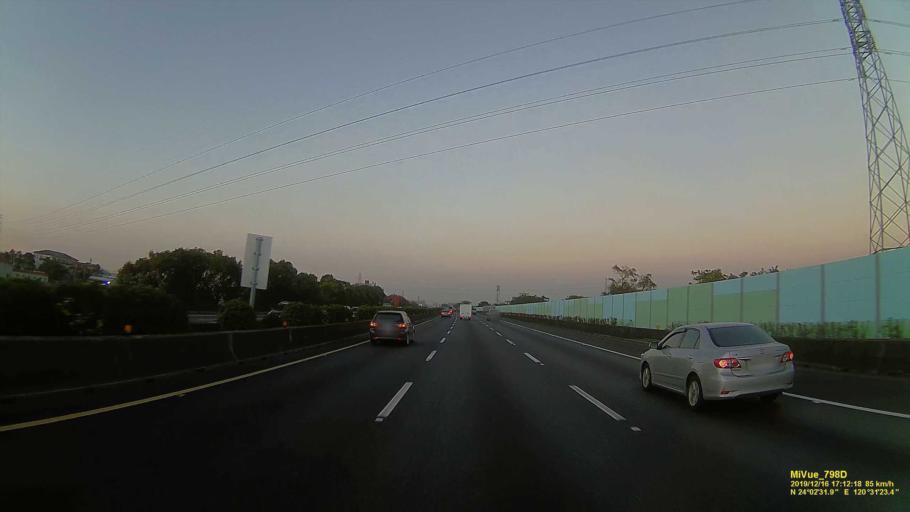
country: TW
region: Taiwan
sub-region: Changhua
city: Chang-hua
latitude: 24.0426
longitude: 120.5232
